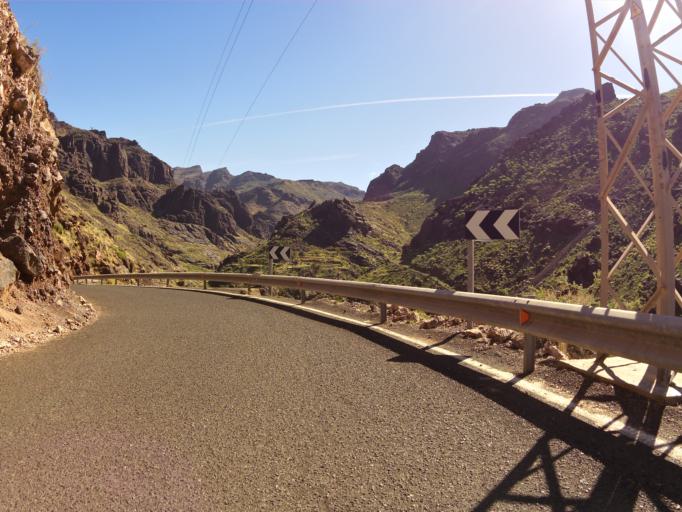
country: ES
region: Canary Islands
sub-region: Provincia de Las Palmas
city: San Nicolas
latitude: 27.9869
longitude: -15.7543
